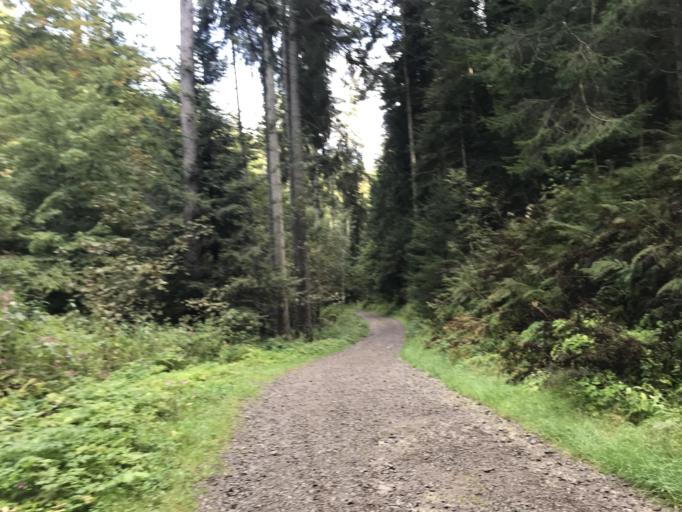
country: DE
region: Baden-Wuerttemberg
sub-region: Karlsruhe Region
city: Calw
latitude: 48.6980
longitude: 8.7229
